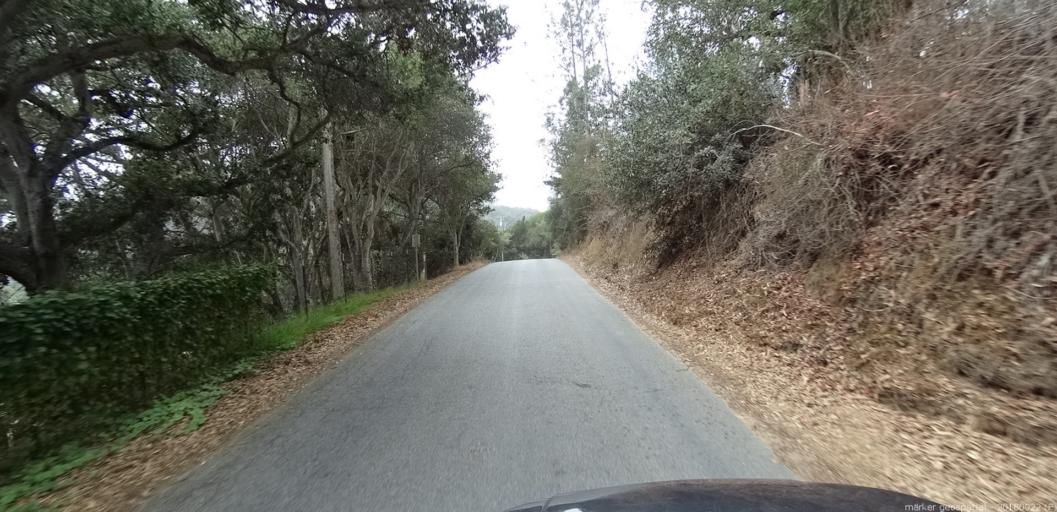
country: US
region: California
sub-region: Monterey County
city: Prunedale
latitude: 36.7906
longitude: -121.6747
